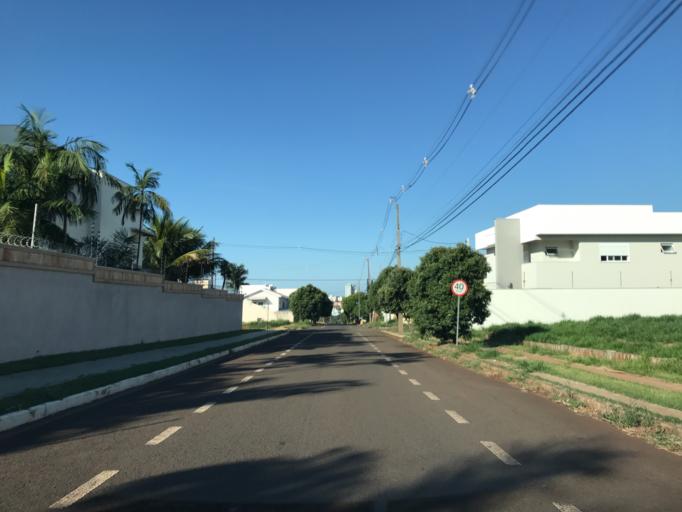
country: BR
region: Parana
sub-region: Maringa
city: Maringa
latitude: -23.4454
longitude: -51.9521
